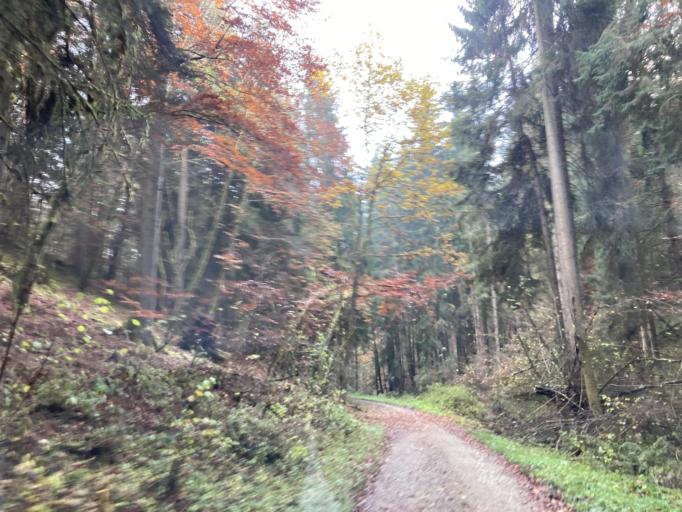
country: DE
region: Baden-Wuerttemberg
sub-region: Regierungsbezirk Stuttgart
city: Bondorf
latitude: 48.4747
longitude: 8.8339
